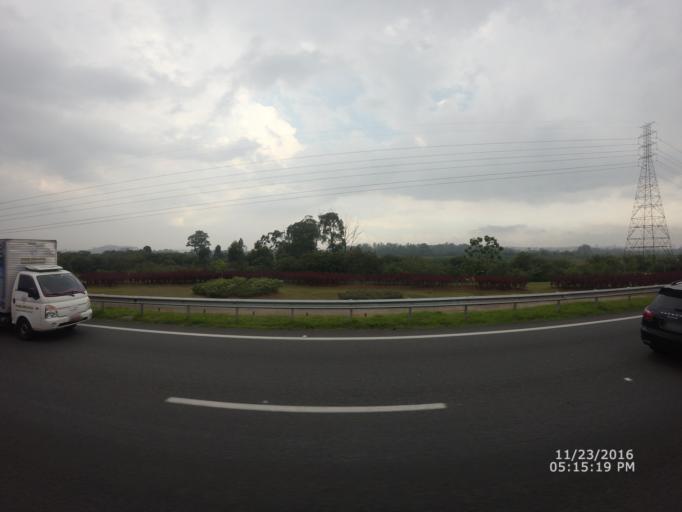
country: BR
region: Sao Paulo
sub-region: Guarulhos
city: Guarulhos
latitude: -23.4801
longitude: -46.5216
